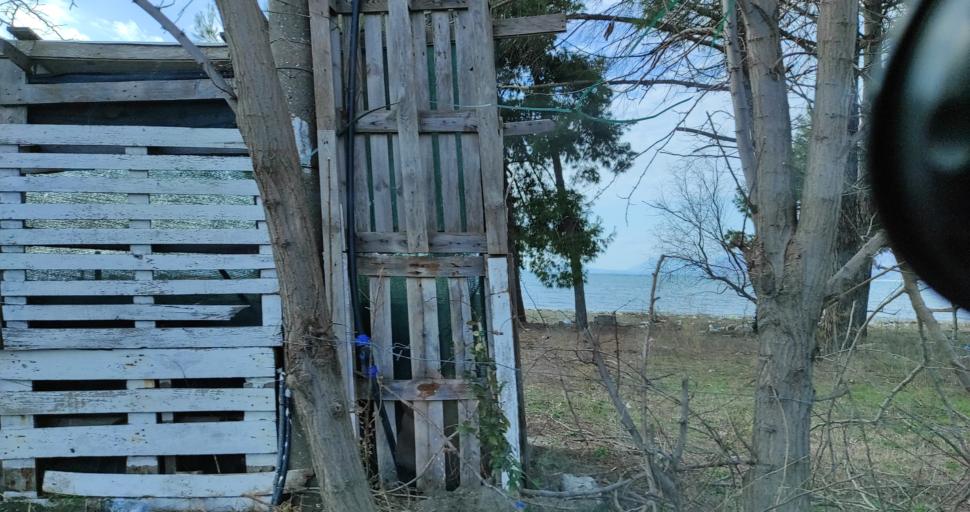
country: AL
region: Lezhe
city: Shengjin
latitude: 41.7689
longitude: 19.5997
